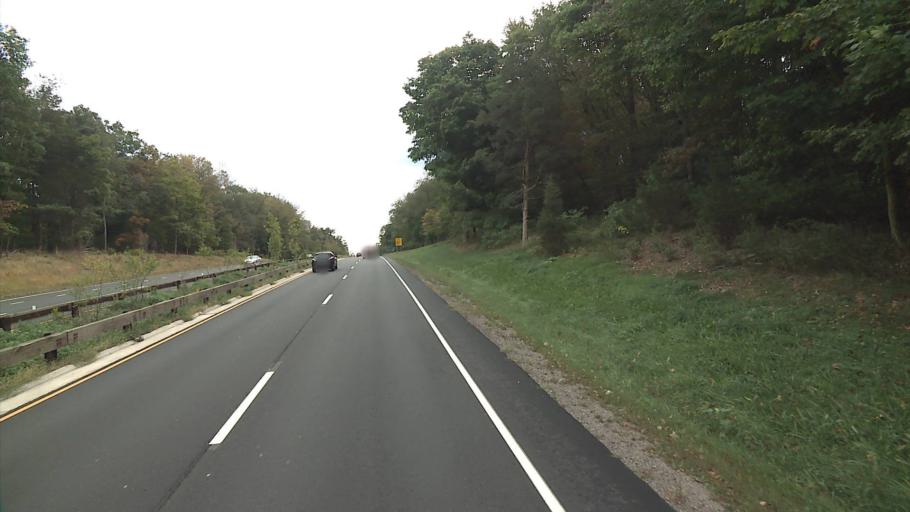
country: US
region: Connecticut
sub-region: Fairfield County
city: North Stamford
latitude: 41.1007
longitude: -73.5802
